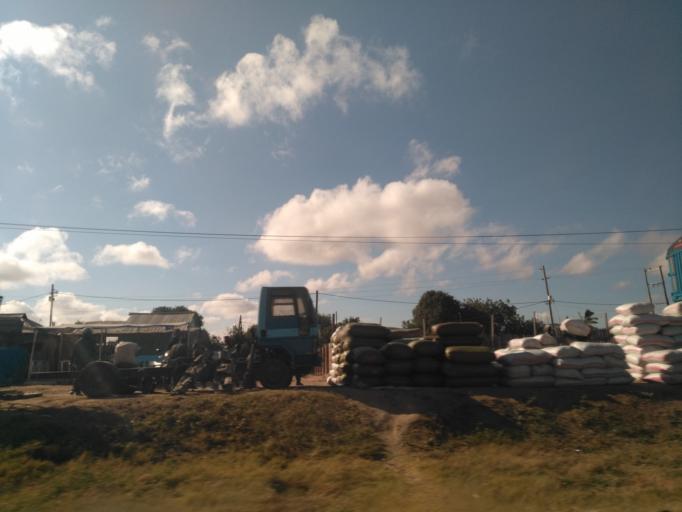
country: TZ
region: Dodoma
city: Dodoma
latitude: -6.1763
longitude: 35.7377
